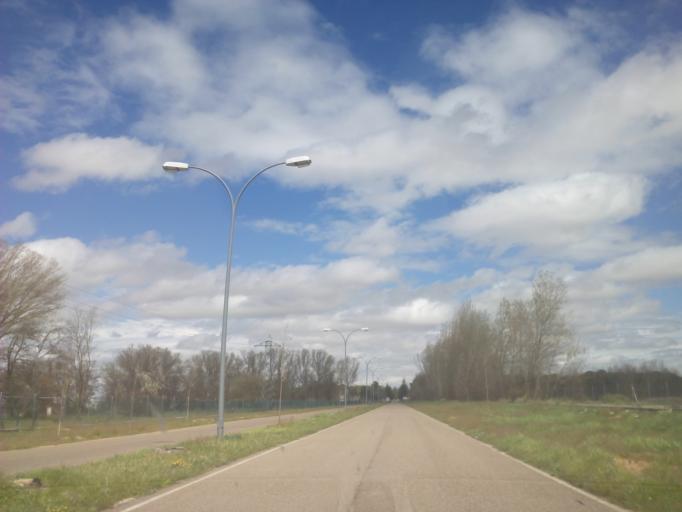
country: ES
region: Castille and Leon
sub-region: Provincia de Salamanca
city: Encinas de Abajo
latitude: 40.9375
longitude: -5.4955
